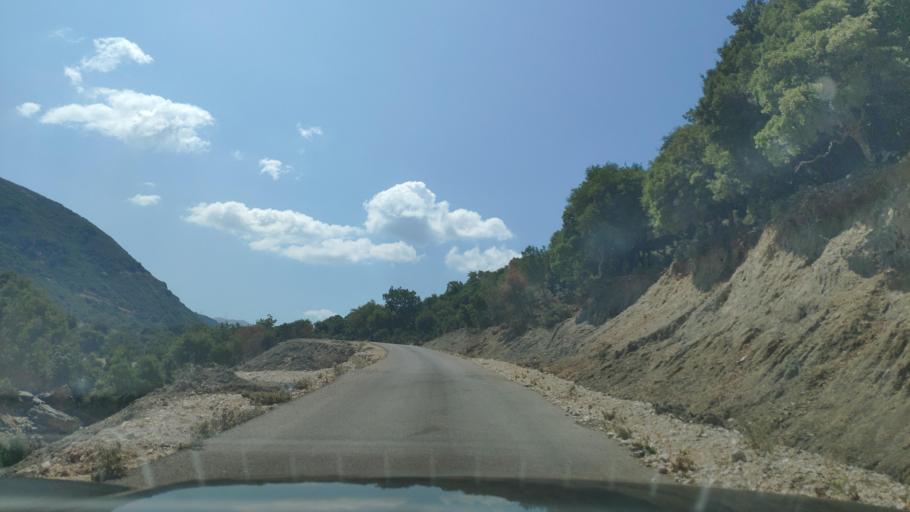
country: GR
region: West Greece
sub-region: Nomos Aitolias kai Akarnanias
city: Monastirakion
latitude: 38.8229
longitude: 20.9287
